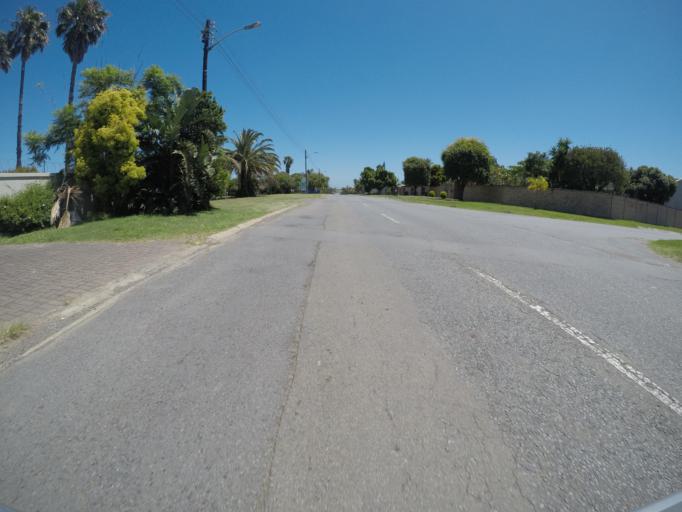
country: ZA
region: Eastern Cape
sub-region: Buffalo City Metropolitan Municipality
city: East London
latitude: -32.9570
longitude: 27.9403
